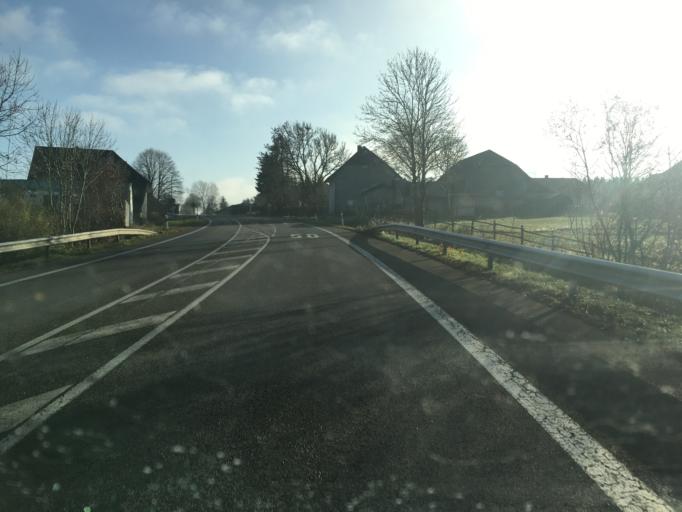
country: DE
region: North Rhine-Westphalia
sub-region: Regierungsbezirk Koln
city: Schleiden
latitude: 50.5612
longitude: 6.4432
